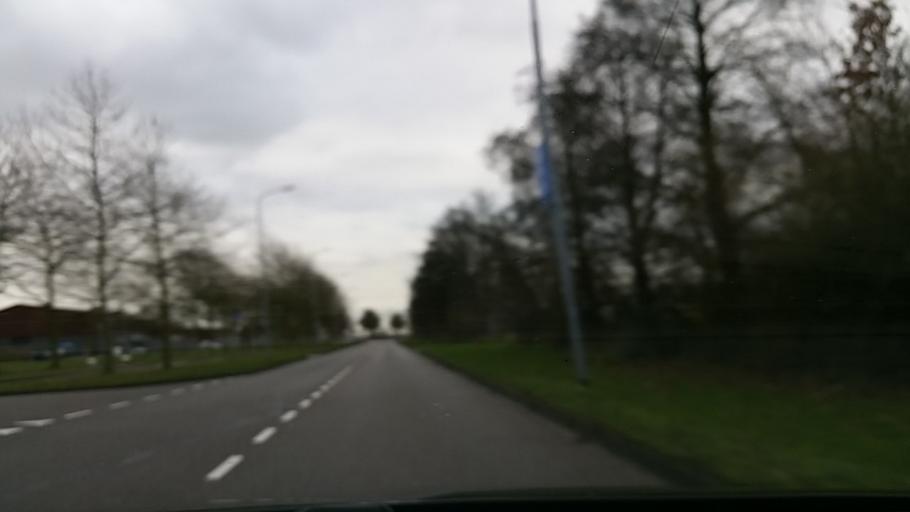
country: NL
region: South Holland
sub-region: Gemeente Kaag en Braassem
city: Leimuiden
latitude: 52.2654
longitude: 4.6441
